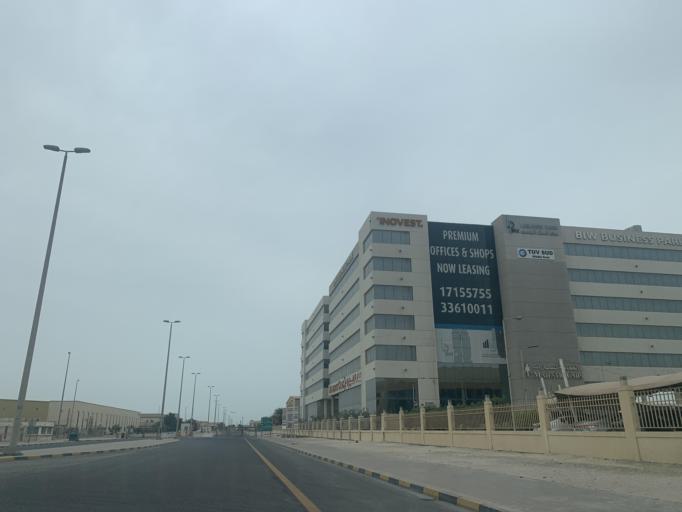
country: BH
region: Muharraq
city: Al Hadd
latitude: 26.2132
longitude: 50.6674
